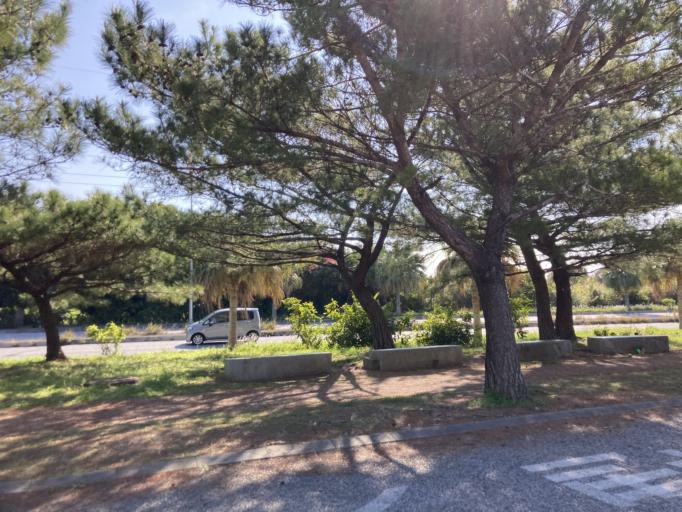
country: JP
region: Okinawa
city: Ishikawa
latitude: 26.3987
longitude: 127.7580
